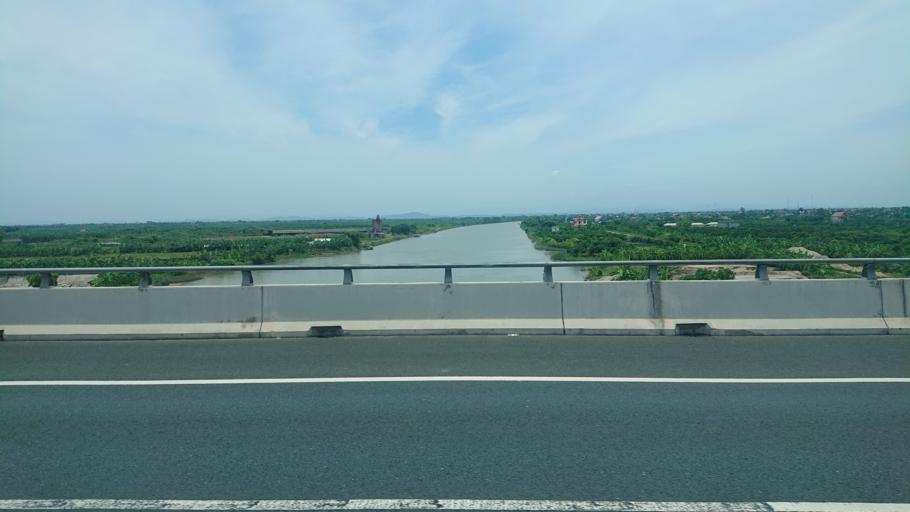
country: VN
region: Hai Duong
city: Tu Ky
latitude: 20.8327
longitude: 106.4428
